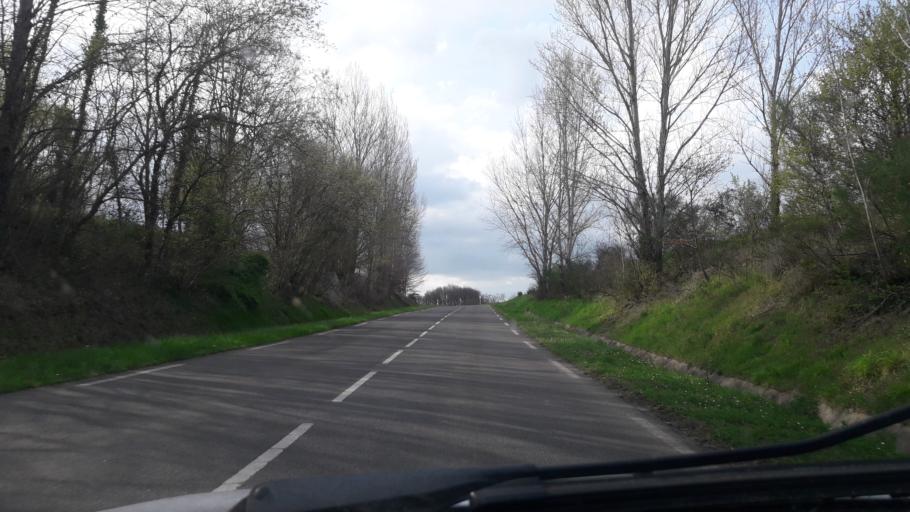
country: FR
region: Midi-Pyrenees
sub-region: Departement de la Haute-Garonne
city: Rieux-Volvestre
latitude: 43.2663
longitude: 1.2025
